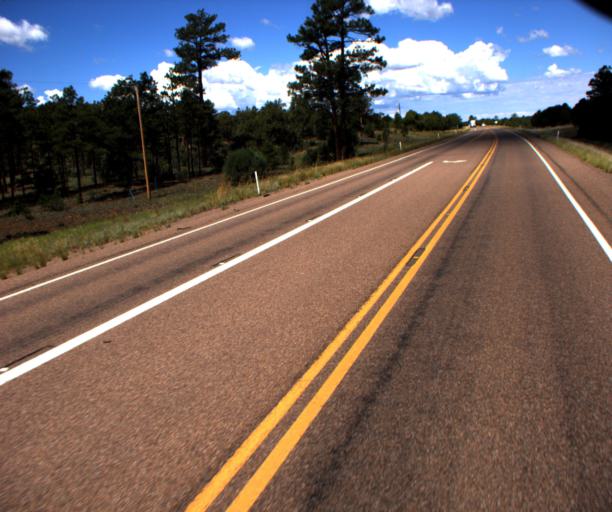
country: US
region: Arizona
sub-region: Navajo County
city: Linden
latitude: 34.3374
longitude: -110.2743
